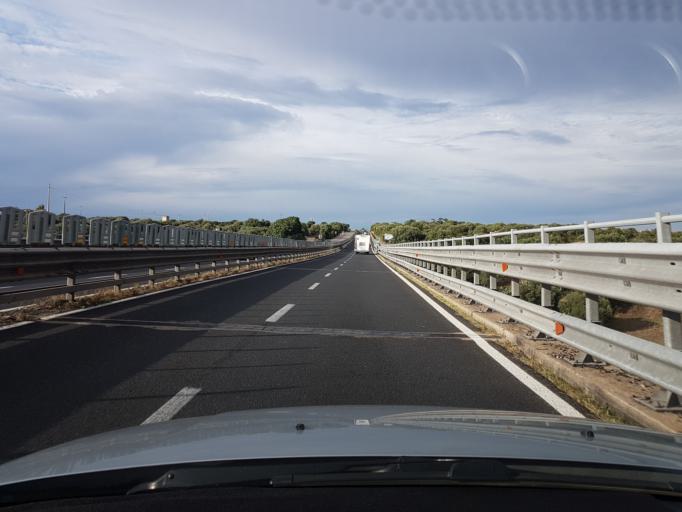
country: IT
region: Sardinia
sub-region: Provincia di Oristano
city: Paulilatino
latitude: 40.0836
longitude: 8.7523
